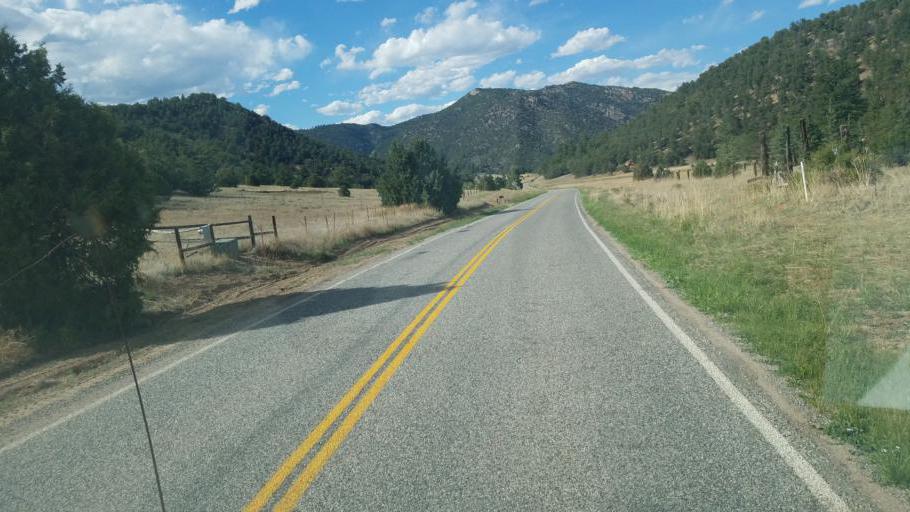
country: US
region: Colorado
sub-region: Fremont County
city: Canon City
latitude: 38.3747
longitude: -105.4565
